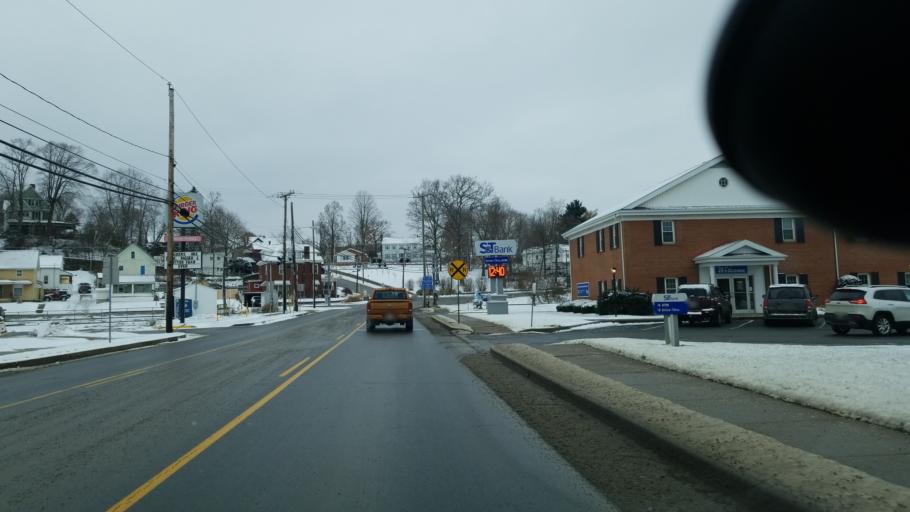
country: US
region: Pennsylvania
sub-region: Jefferson County
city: Punxsutawney
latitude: 40.9465
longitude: -78.9676
